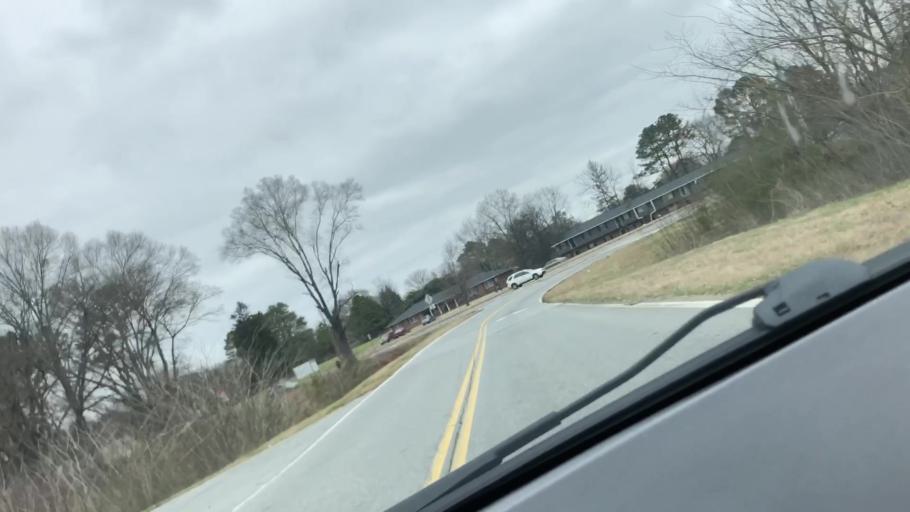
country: US
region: Georgia
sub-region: Bartow County
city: Cartersville
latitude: 34.2069
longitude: -84.8219
